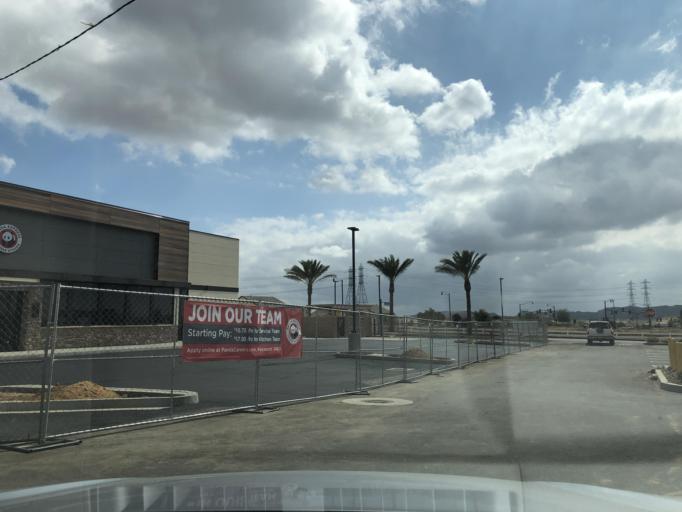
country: US
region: California
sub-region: Riverside County
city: Calimesa
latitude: 33.9659
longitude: -117.0343
